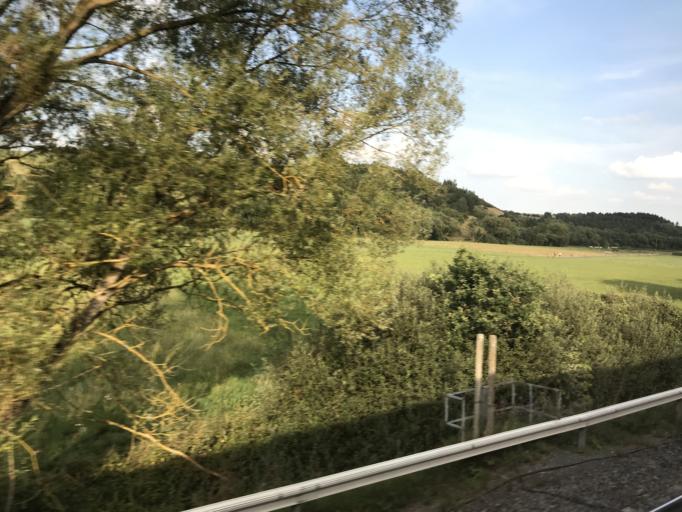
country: DE
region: Hesse
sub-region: Regierungsbezirk Giessen
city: Runkel
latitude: 50.3687
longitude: 8.1361
